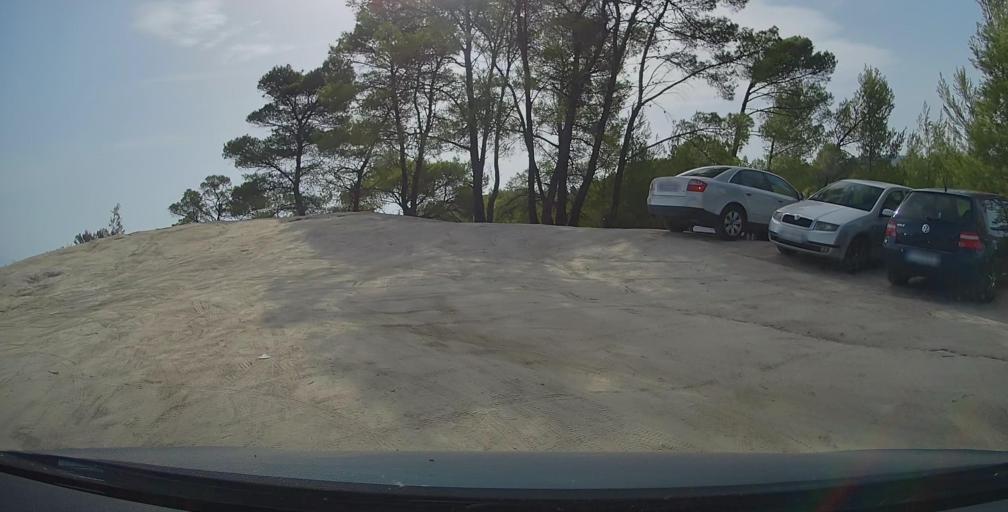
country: GR
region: Central Macedonia
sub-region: Nomos Chalkidikis
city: Sarti
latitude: 40.1296
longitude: 23.9579
